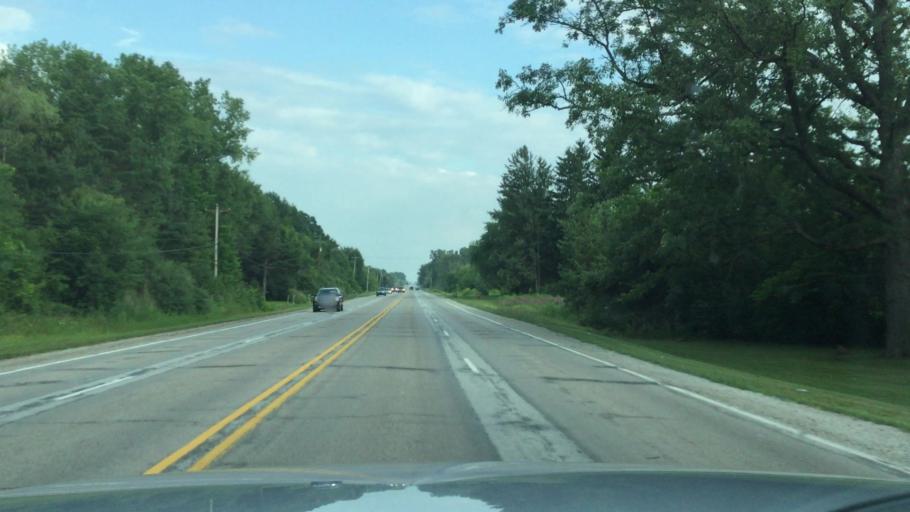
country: US
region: Michigan
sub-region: Saginaw County
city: Birch Run
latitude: 43.2764
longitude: -83.7891
